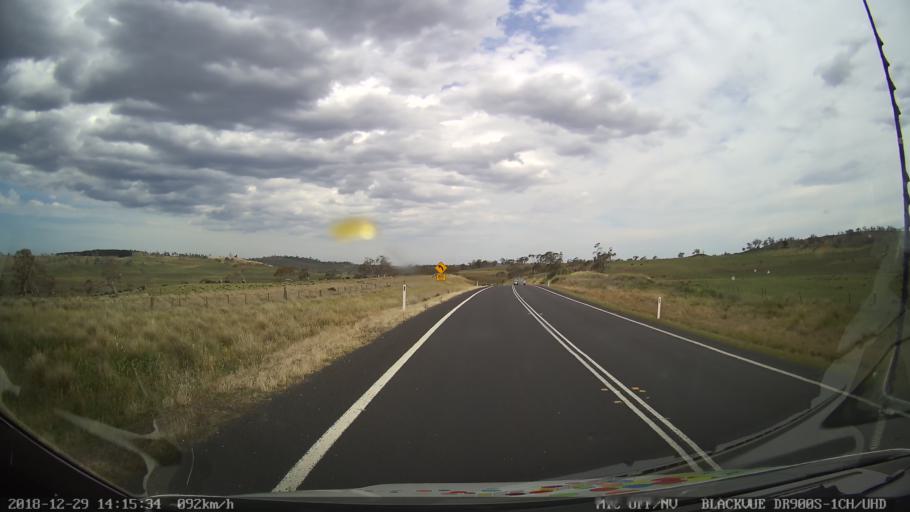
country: AU
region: New South Wales
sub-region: Cooma-Monaro
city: Cooma
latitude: -36.4574
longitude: 149.2421
